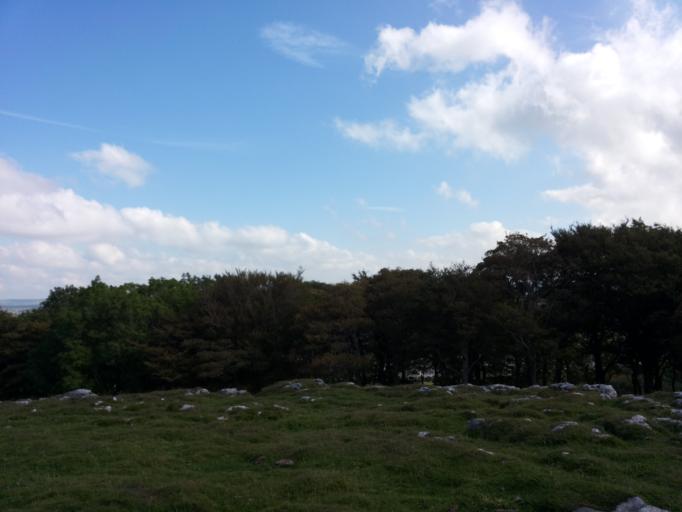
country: GB
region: England
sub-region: Derbyshire
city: Buxton
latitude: 53.2424
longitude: -1.9201
